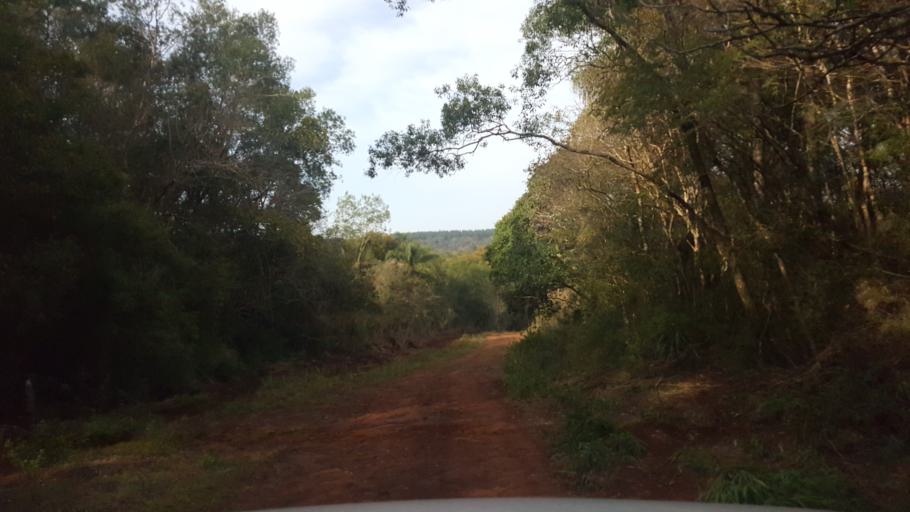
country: AR
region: Misiones
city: Capiovi
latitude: -26.9019
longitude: -55.1060
